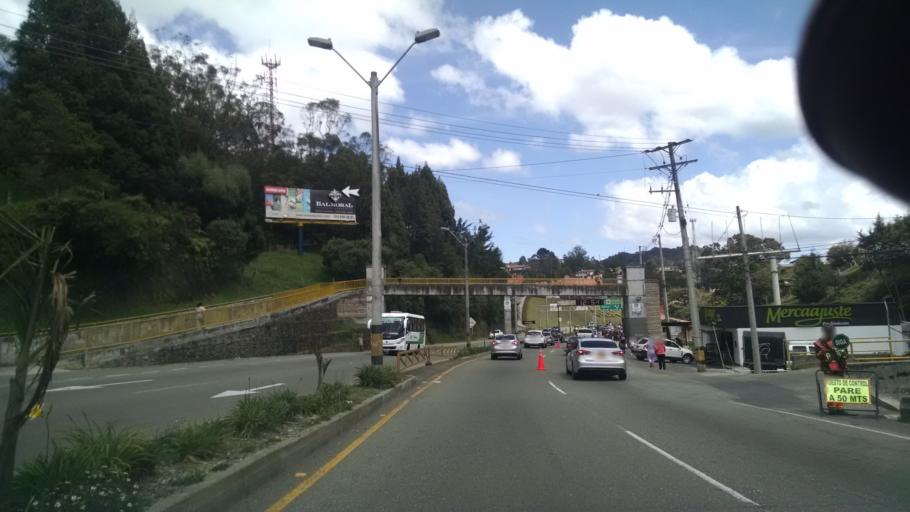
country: CO
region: Antioquia
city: Envigado
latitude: 6.1543
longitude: -75.5361
